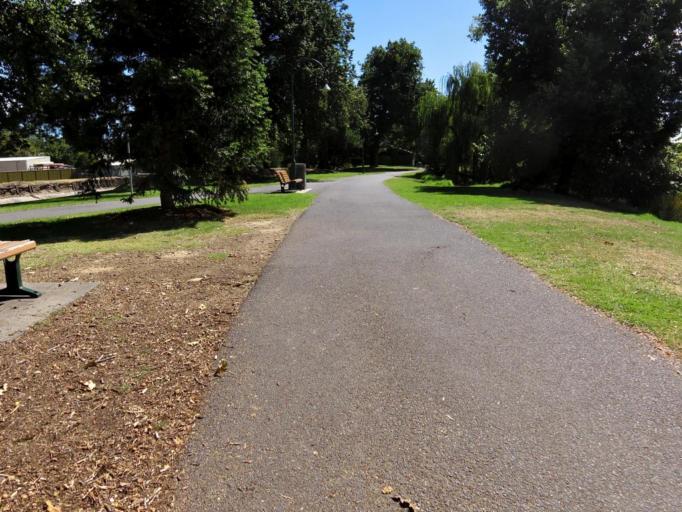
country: AU
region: Victoria
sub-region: Greater Bendigo
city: Bendigo
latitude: -36.7480
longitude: 144.2895
